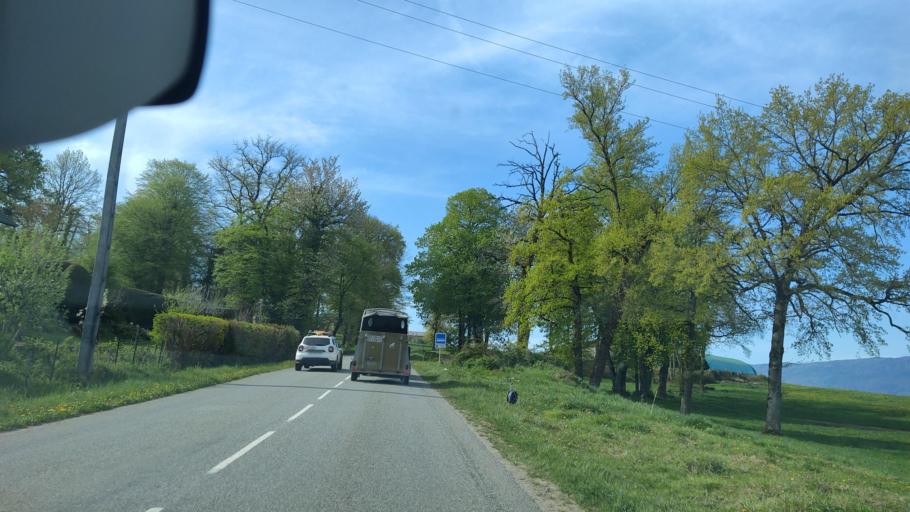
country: FR
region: Rhone-Alpes
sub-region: Departement de la Savoie
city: Gresy-sur-Aix
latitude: 45.7107
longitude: 5.9527
